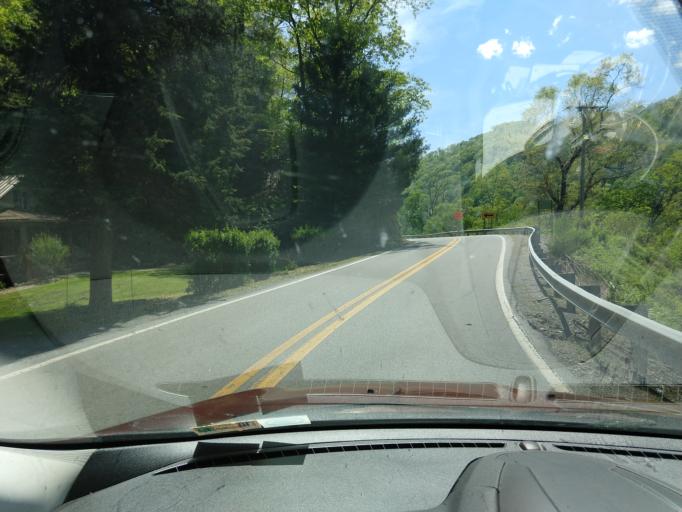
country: US
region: West Virginia
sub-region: McDowell County
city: Welch
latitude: 37.3120
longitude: -81.6936
